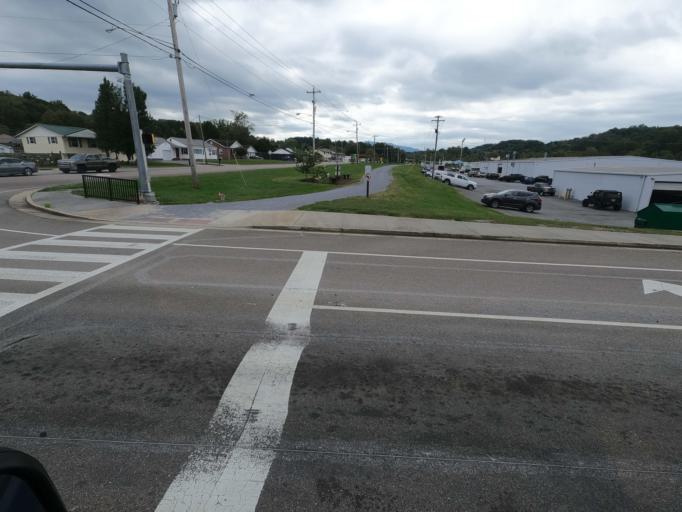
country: US
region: Tennessee
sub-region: Carter County
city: Central
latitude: 36.3311
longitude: -82.2645
